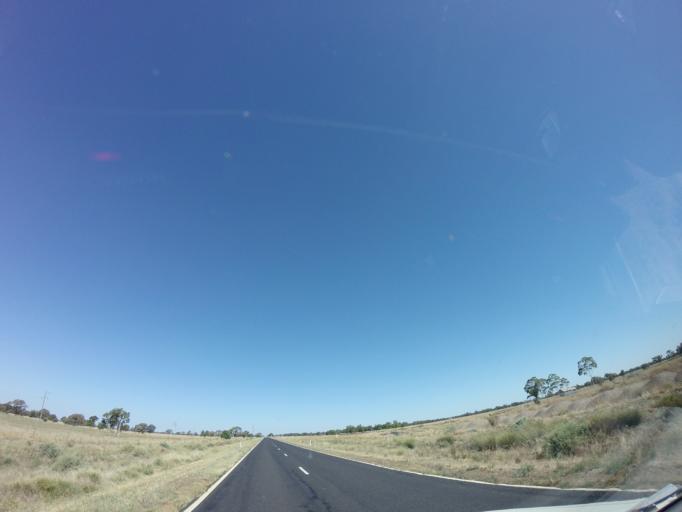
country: AU
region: New South Wales
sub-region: Bogan
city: Nyngan
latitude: -31.6873
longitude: 147.4325
